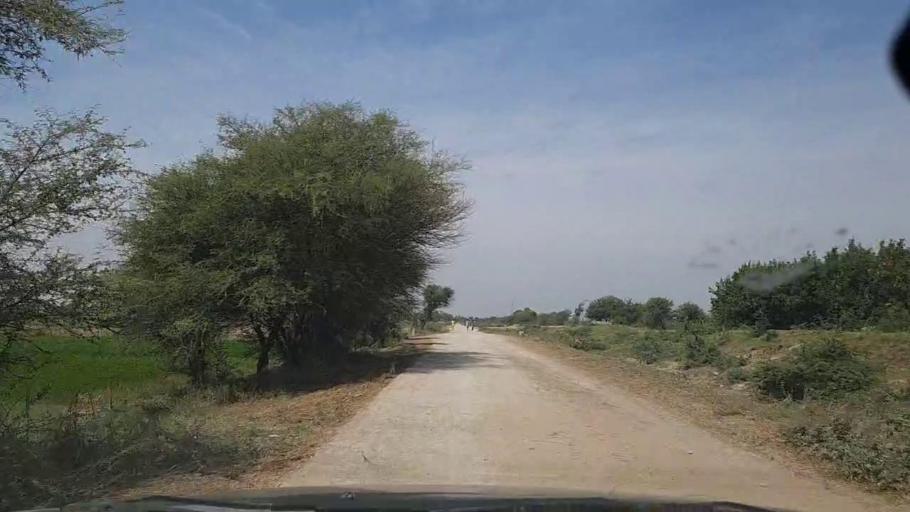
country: PK
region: Sindh
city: Mirpur Batoro
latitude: 24.6479
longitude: 68.1873
